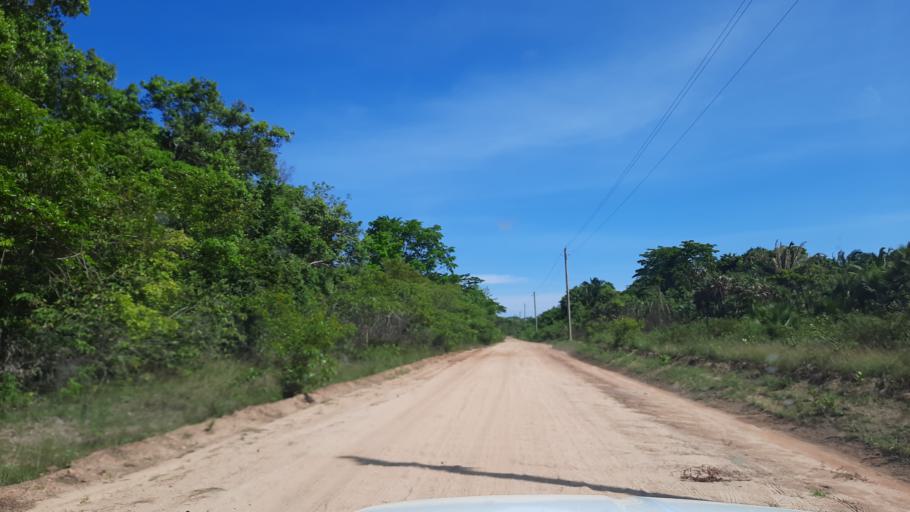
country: BZ
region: Stann Creek
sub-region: Dangriga
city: Dangriga
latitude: 17.1628
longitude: -88.3290
